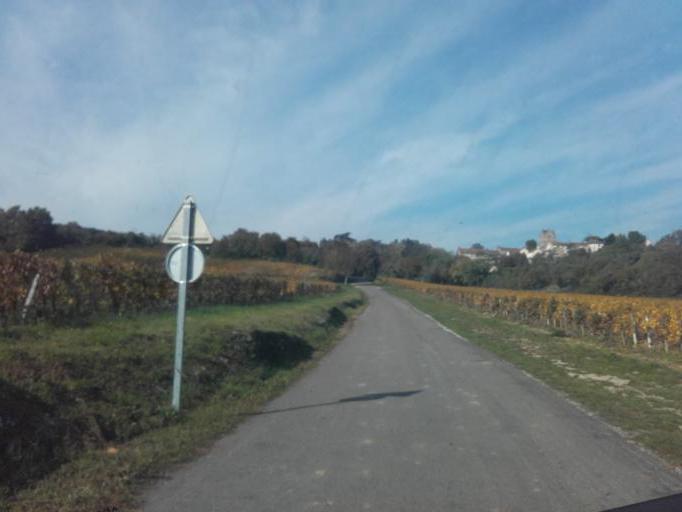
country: FR
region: Bourgogne
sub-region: Departement de Saone-et-Loire
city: Mellecey
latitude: 46.8273
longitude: 4.7196
